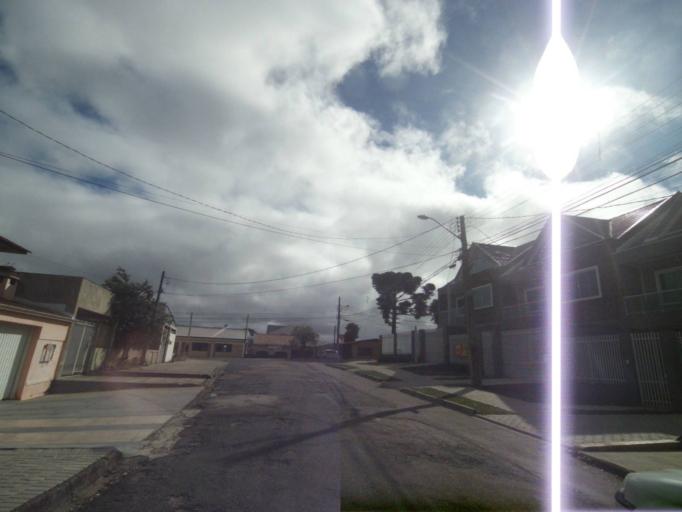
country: BR
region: Parana
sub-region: Sao Jose Dos Pinhais
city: Sao Jose dos Pinhais
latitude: -25.5200
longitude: -49.3016
